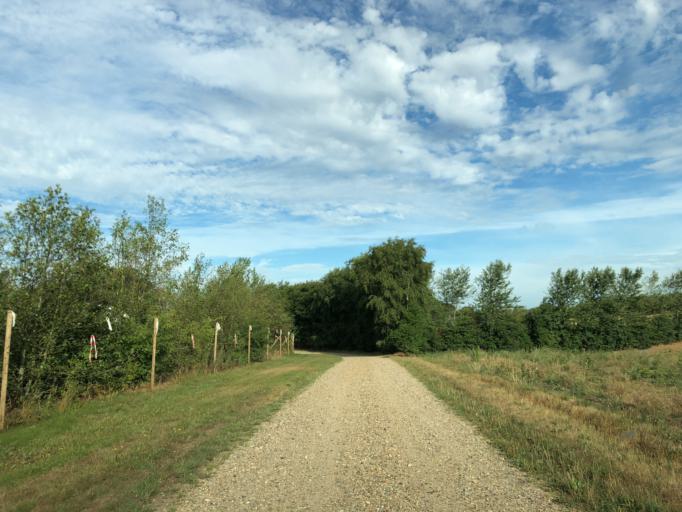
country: DK
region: Central Jutland
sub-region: Ringkobing-Skjern Kommune
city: Skjern
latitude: 56.0401
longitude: 8.4373
